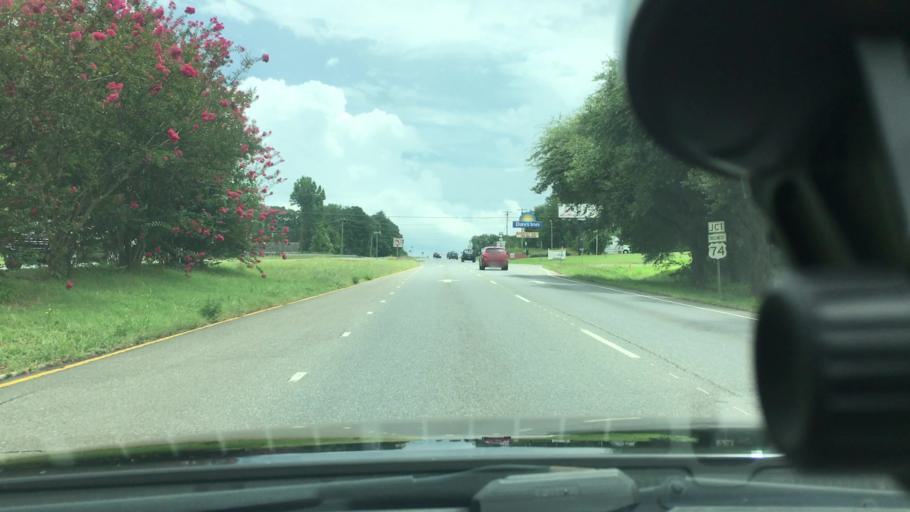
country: US
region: North Carolina
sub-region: Cleveland County
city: Shelby
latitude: 35.2917
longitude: -81.5656
